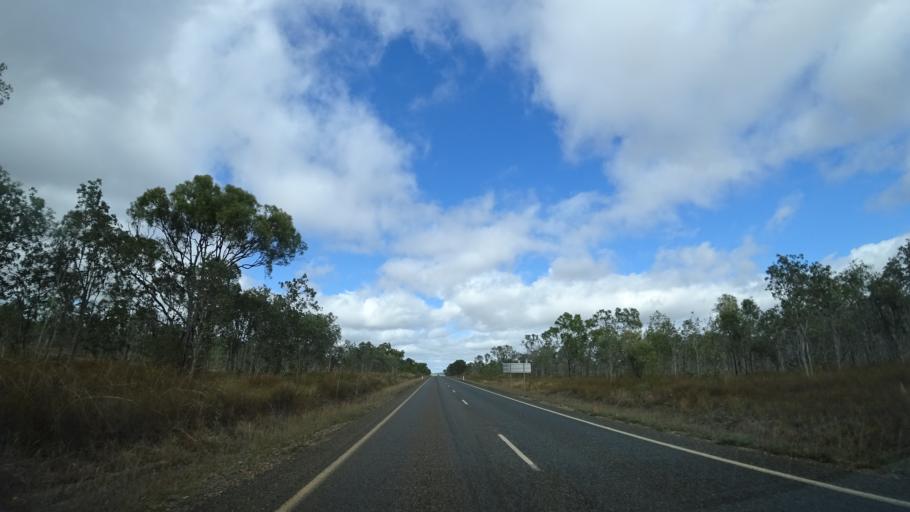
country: AU
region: Queensland
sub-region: Cook
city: Cooktown
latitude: -15.8797
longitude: 144.8600
